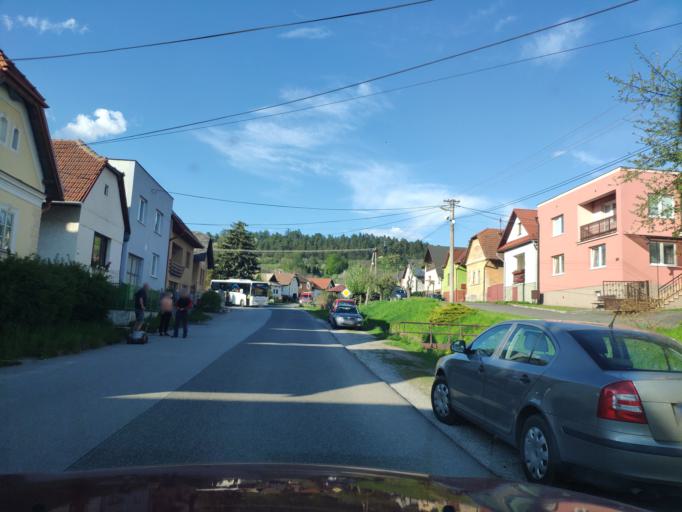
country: SK
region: Presovsky
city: Spisske Podhradie
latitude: 49.0238
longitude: 20.7986
